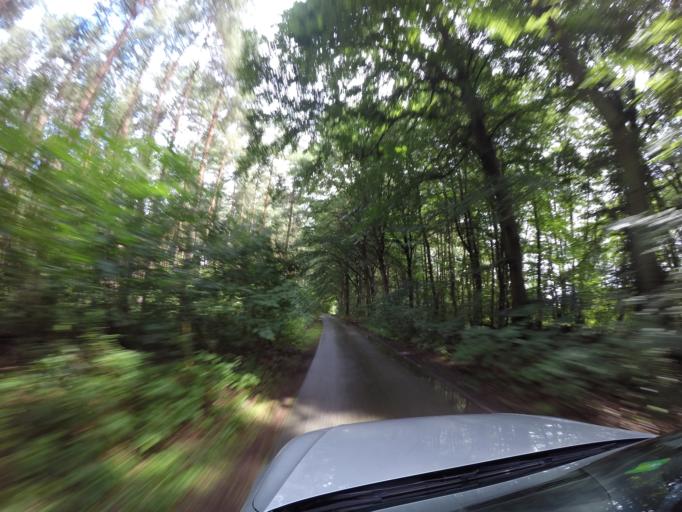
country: DE
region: Mecklenburg-Vorpommern
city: Rechlin
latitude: 53.3576
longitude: 12.8580
